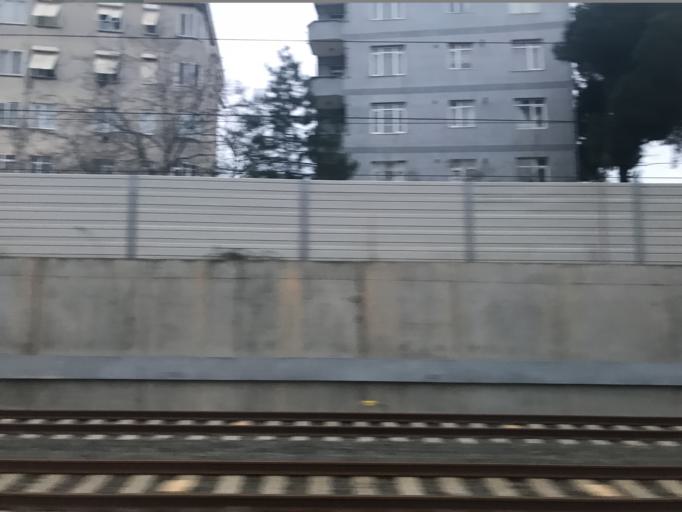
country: TR
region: Istanbul
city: Icmeler
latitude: 40.8306
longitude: 29.3212
